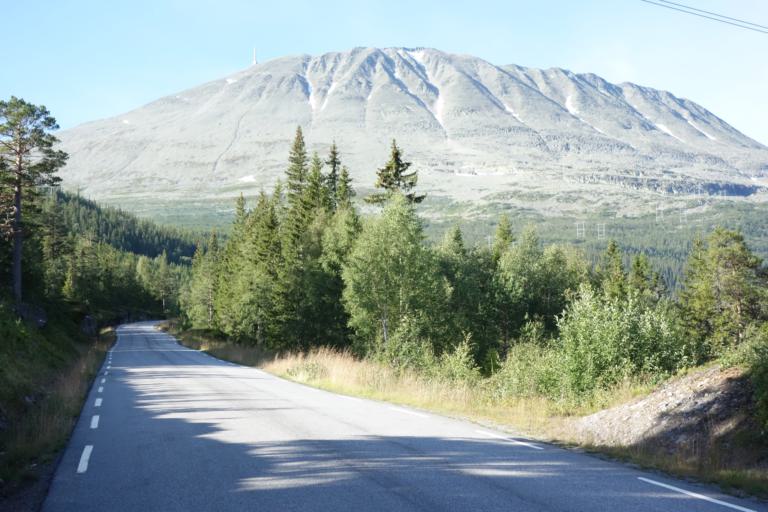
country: NO
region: Telemark
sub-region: Tinn
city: Rjukan
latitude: 59.8793
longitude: 8.6986
